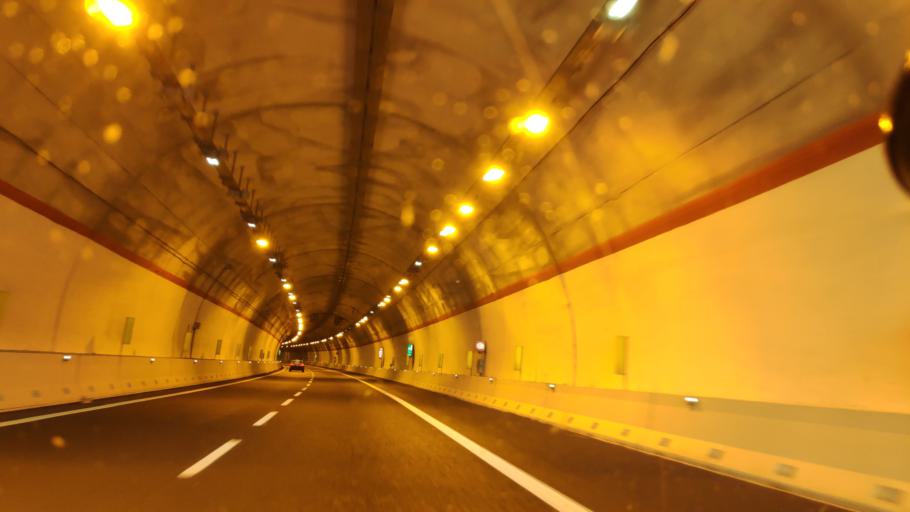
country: IT
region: Campania
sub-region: Provincia di Salerno
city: Casalbuono
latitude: 40.2133
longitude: 15.6732
